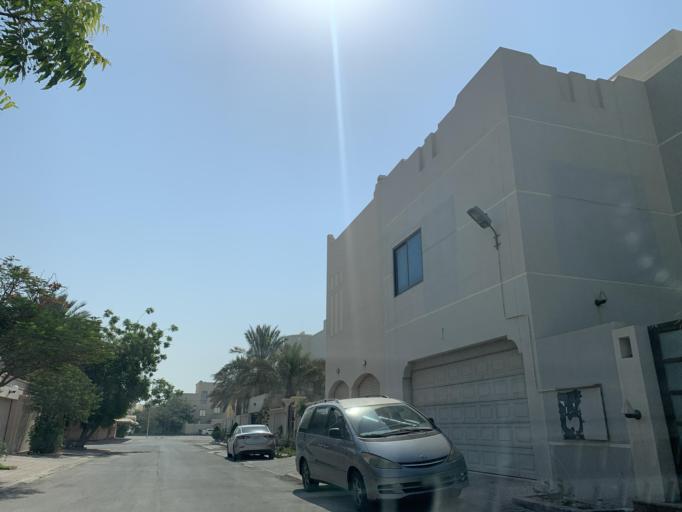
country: BH
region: Northern
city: Madinat `Isa
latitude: 26.1957
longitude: 50.5126
